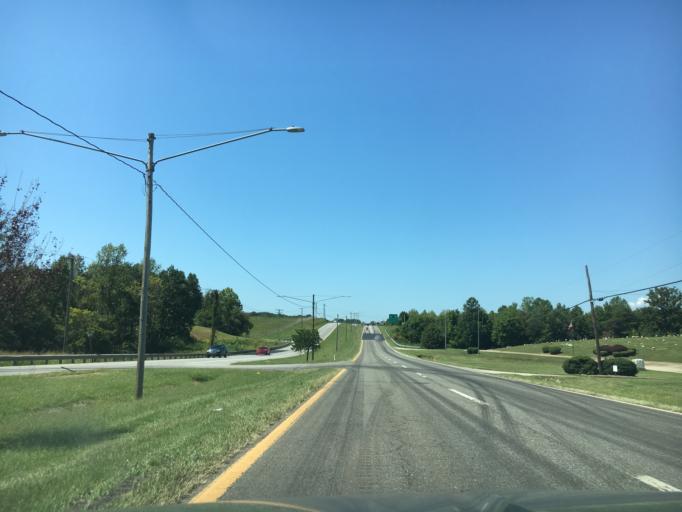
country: US
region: Virginia
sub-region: City of Danville
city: Danville
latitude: 36.5810
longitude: -79.3276
